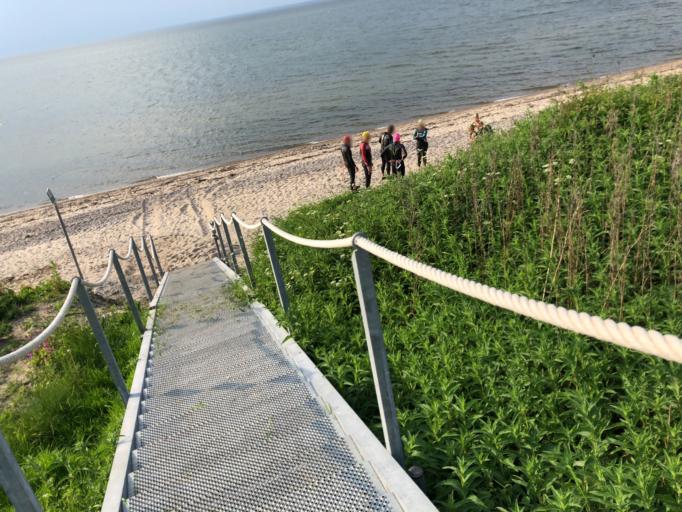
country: DK
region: Central Jutland
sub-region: Struer Kommune
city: Struer
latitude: 56.5429
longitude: 8.5238
